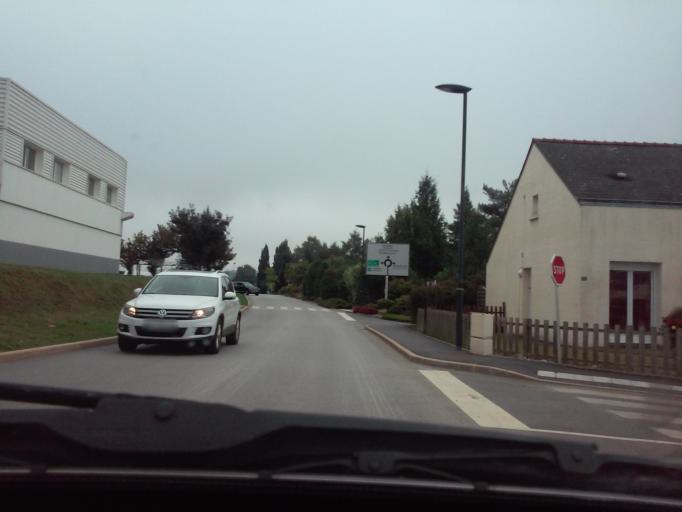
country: FR
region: Brittany
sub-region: Departement du Morbihan
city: Josselin
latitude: 47.9616
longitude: -2.5480
